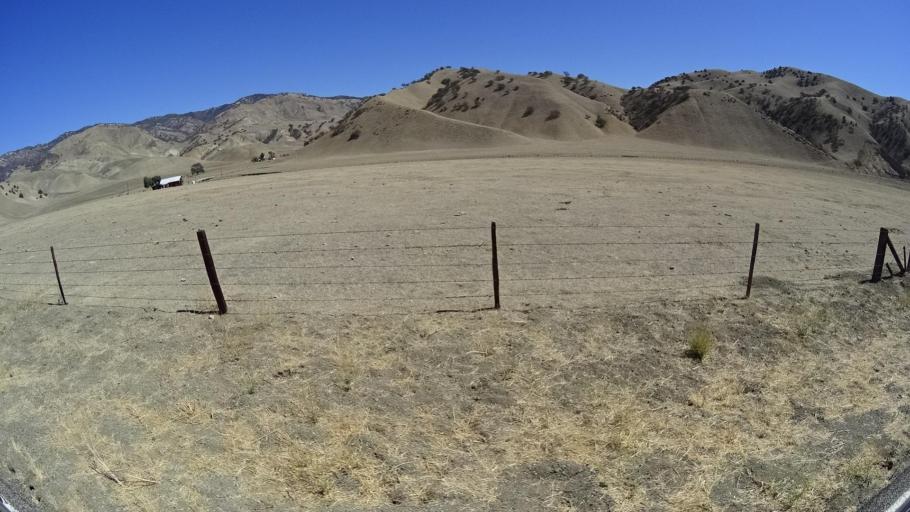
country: US
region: California
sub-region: Monterey County
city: King City
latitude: 36.3078
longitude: -120.9297
